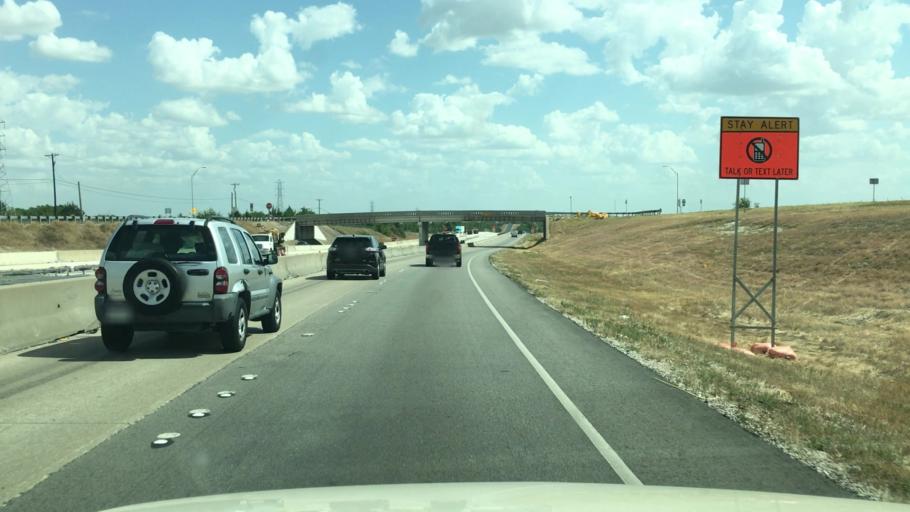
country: US
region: Texas
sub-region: Ellis County
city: Waxahachie
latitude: 32.3591
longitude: -96.8552
